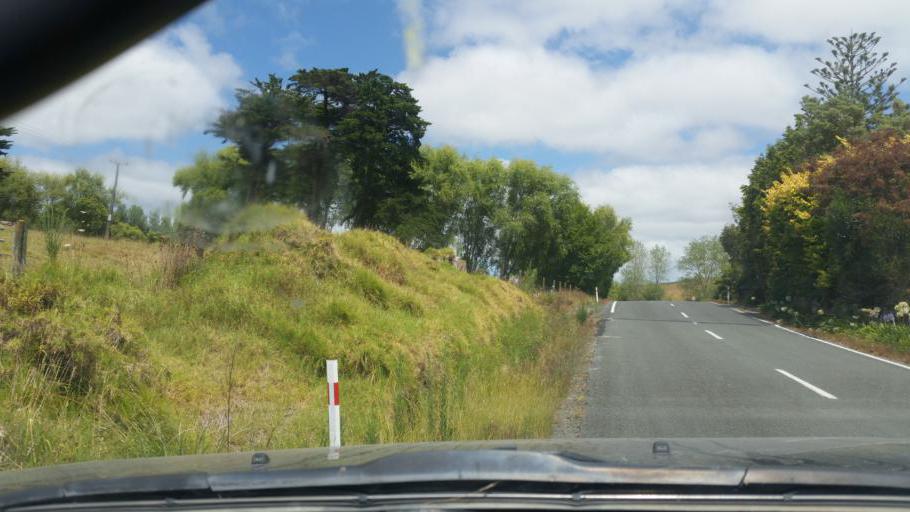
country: NZ
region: Auckland
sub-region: Auckland
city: Wellsford
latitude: -36.1241
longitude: 174.3307
